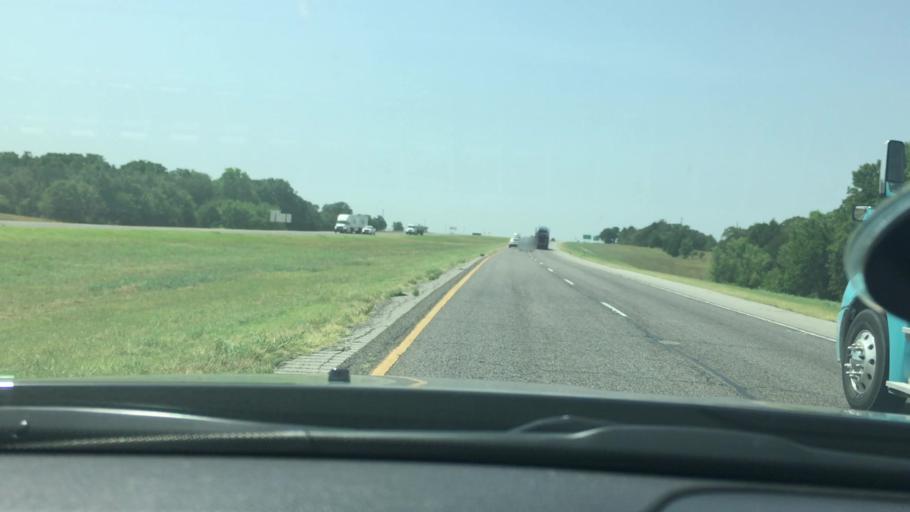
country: US
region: Oklahoma
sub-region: Garvin County
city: Wynnewood
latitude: 34.6352
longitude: -97.2179
